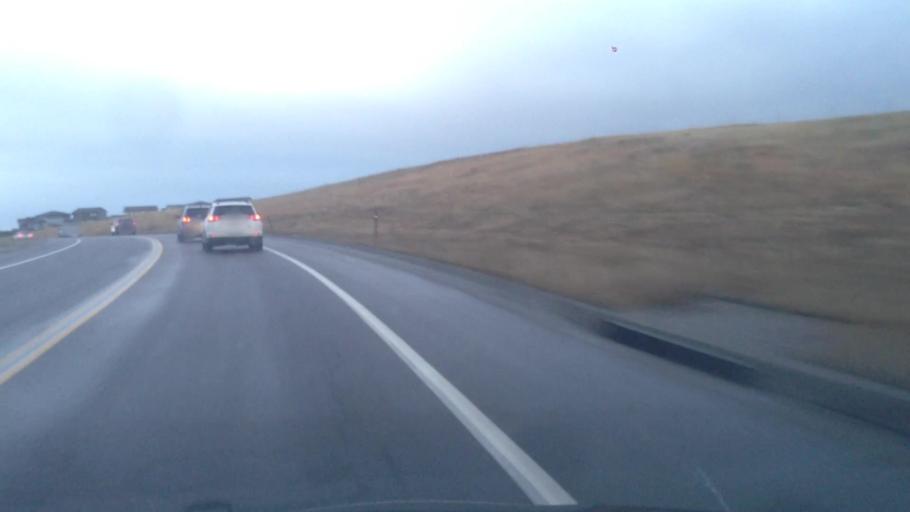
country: US
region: Colorado
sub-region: Douglas County
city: Stonegate
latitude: 39.5198
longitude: -104.8335
